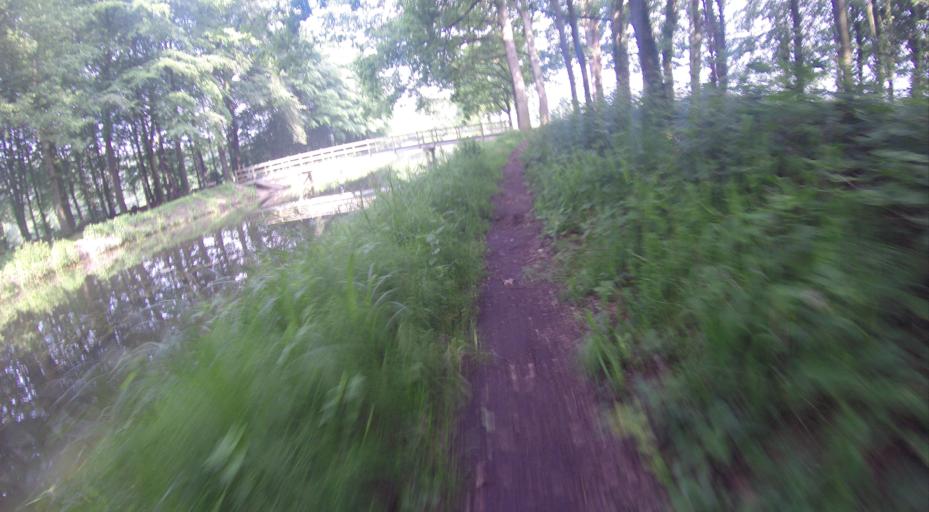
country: NL
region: Gelderland
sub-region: Gemeente Bronckhorst
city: Hengelo
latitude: 52.0960
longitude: 6.3171
